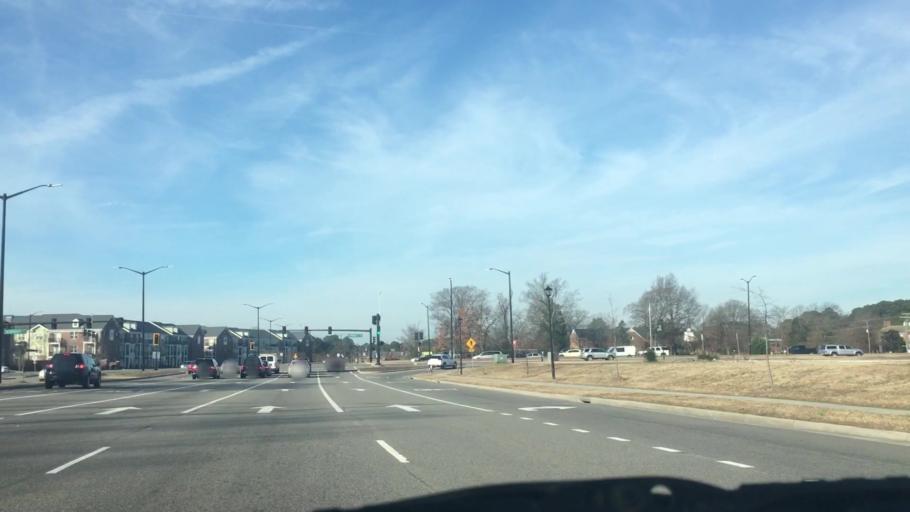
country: US
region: Virginia
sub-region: City of Chesapeake
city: Chesapeake
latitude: 36.8253
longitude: -76.1594
